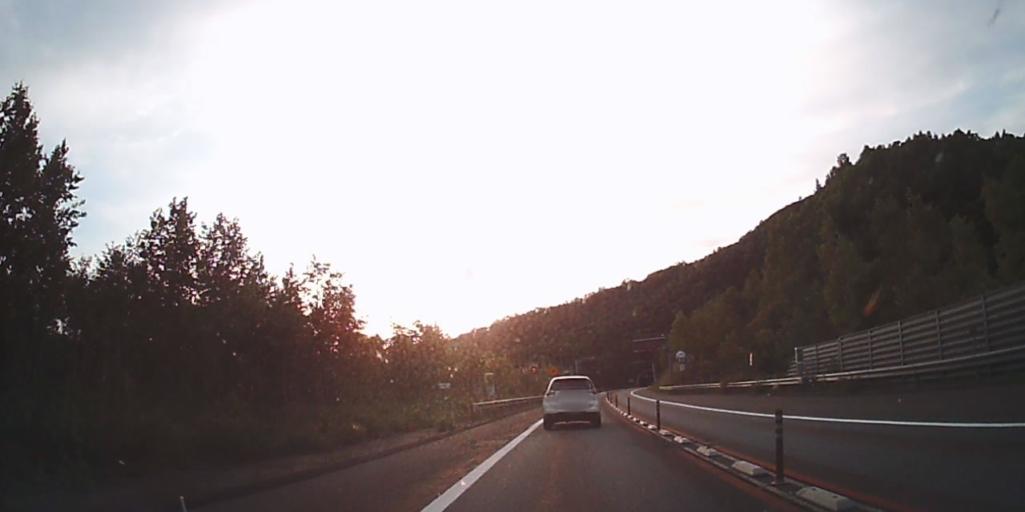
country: JP
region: Hokkaido
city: Date
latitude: 42.5761
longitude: 140.7344
